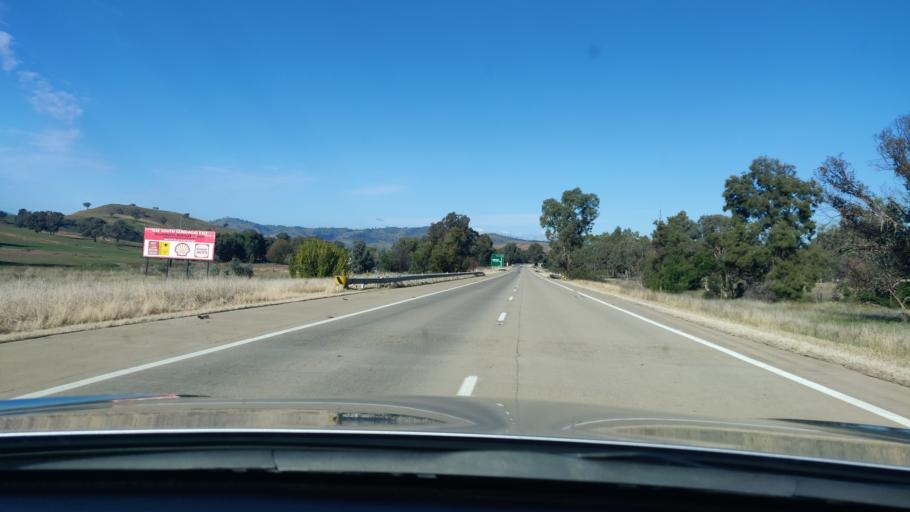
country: AU
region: New South Wales
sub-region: Gundagai
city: Gundagai
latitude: -35.0326
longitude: 148.1103
